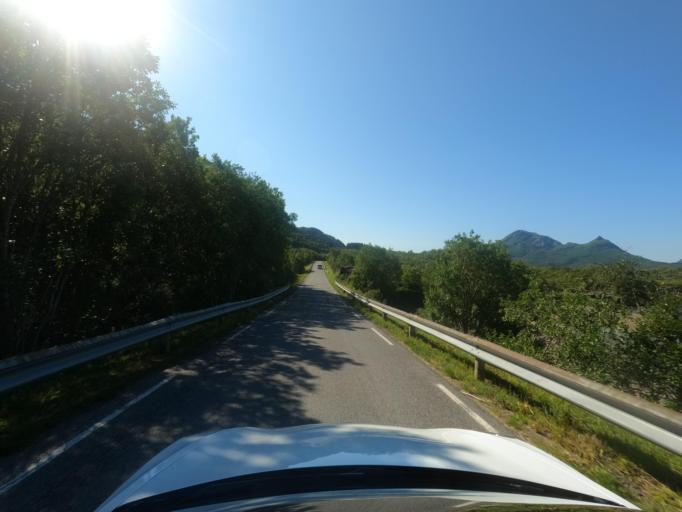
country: NO
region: Nordland
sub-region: Hadsel
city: Stokmarknes
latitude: 68.3232
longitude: 15.0060
